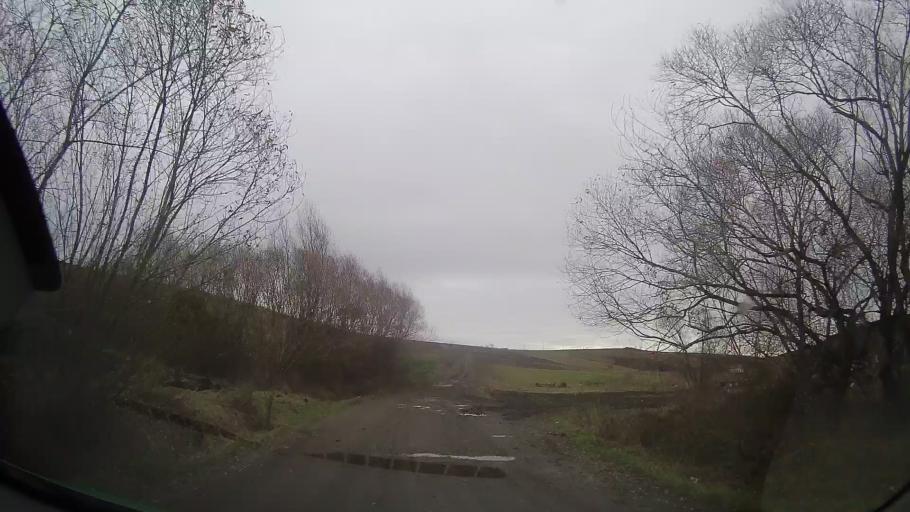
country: RO
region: Mures
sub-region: Comuna Bala
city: Bala
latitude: 46.6948
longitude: 24.4893
